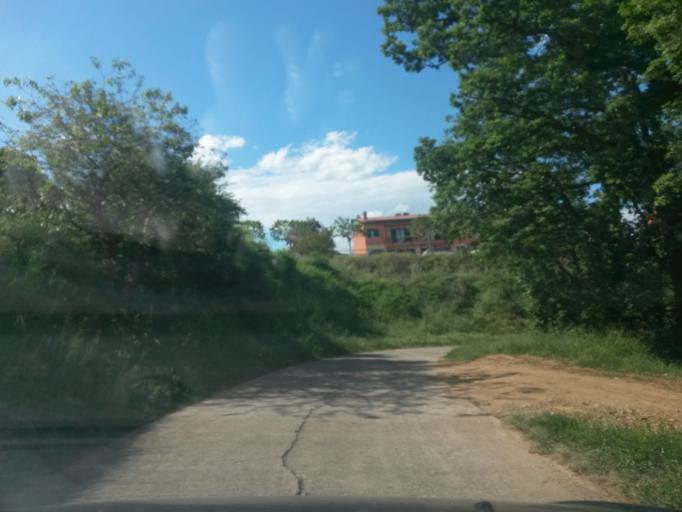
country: ES
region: Catalonia
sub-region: Provincia de Girona
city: Brunyola
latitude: 41.9045
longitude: 2.6855
